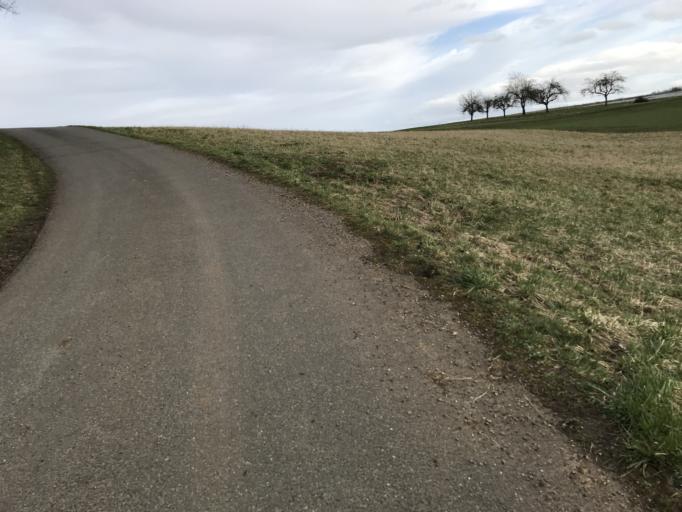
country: DE
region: Hesse
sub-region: Regierungsbezirk Giessen
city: Heuchelheim
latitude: 50.6332
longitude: 8.5764
